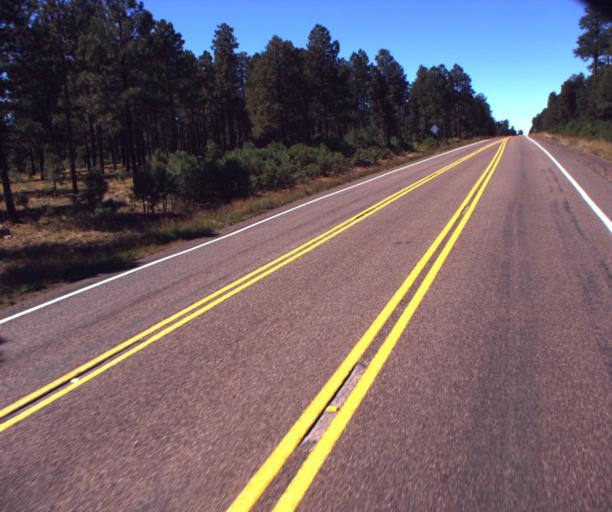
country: US
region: Arizona
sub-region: Navajo County
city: Heber-Overgaard
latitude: 34.3296
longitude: -110.8044
